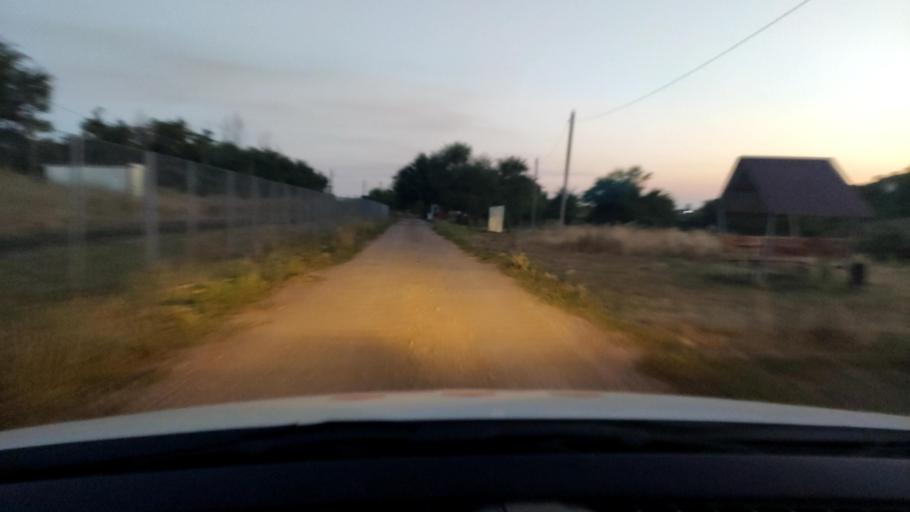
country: RU
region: Voronezj
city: Panino
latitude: 51.6568
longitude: 40.0255
